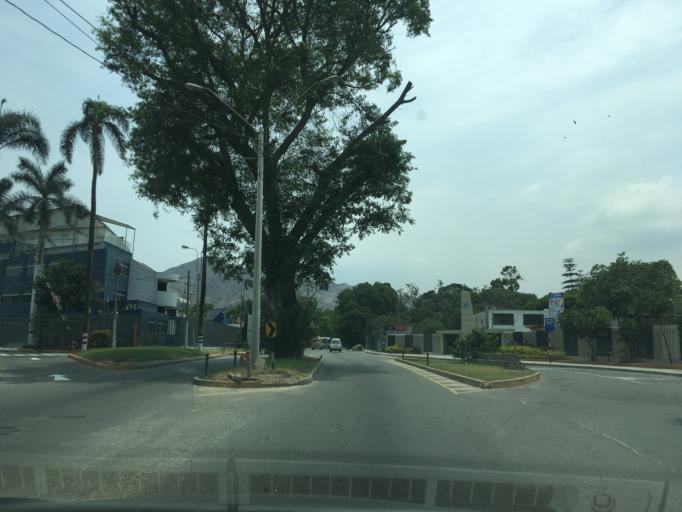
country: PE
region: Lima
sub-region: Lima
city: La Molina
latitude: -12.0785
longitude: -76.9472
